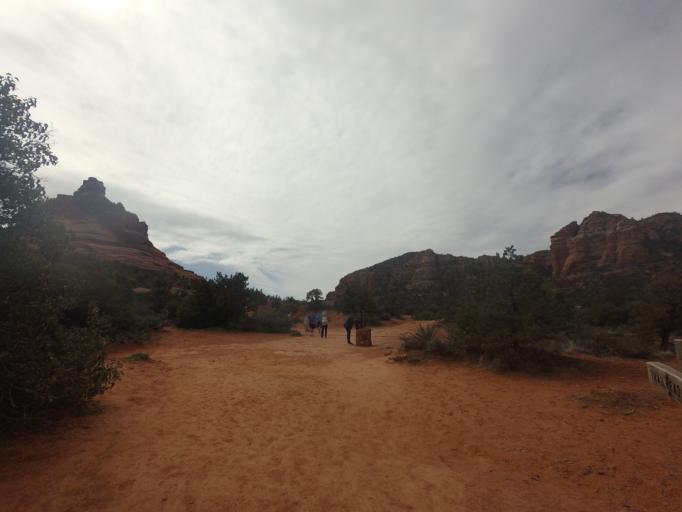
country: US
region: Arizona
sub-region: Yavapai County
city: Village of Oak Creek (Big Park)
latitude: 34.8038
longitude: -111.7660
